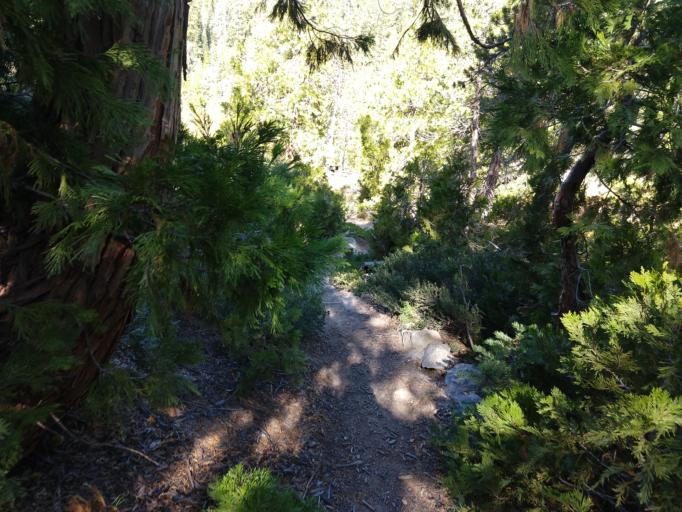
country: US
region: California
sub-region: Plumas County
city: Chester
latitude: 40.4413
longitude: -121.4334
